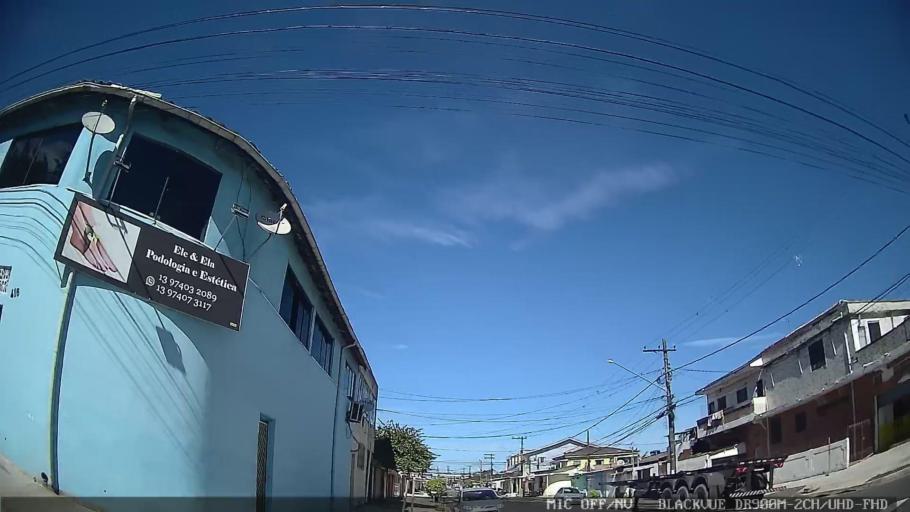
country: BR
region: Sao Paulo
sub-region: Santos
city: Santos
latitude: -23.9494
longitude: -46.2980
